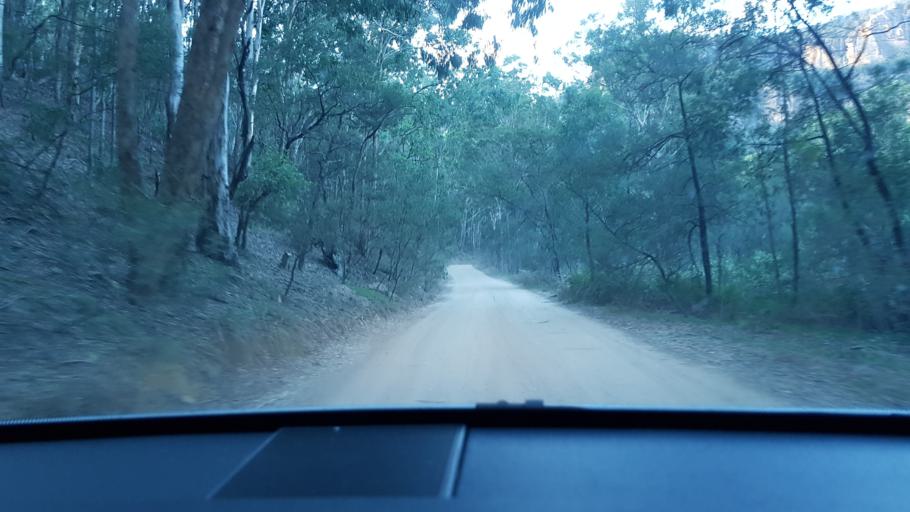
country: AU
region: New South Wales
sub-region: Lithgow
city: Portland
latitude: -33.1772
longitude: 150.2360
